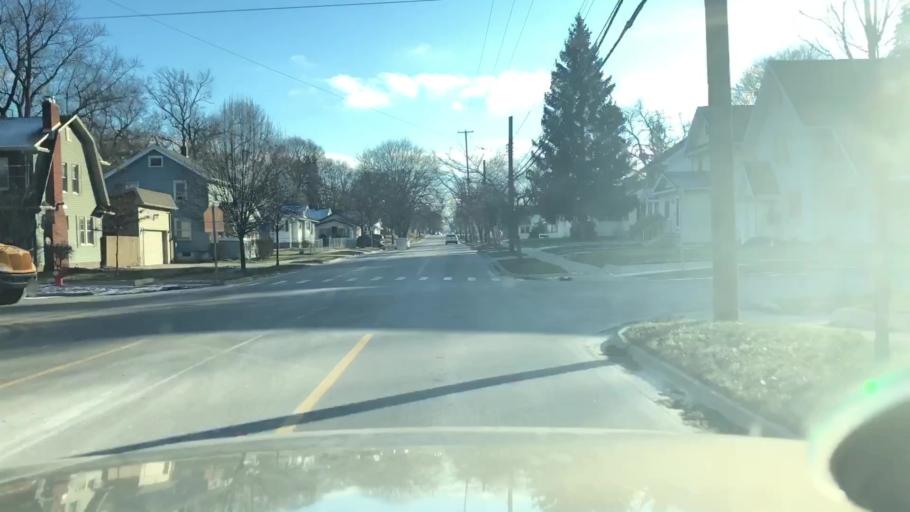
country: US
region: Michigan
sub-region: Jackson County
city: Jackson
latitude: 42.2366
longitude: -84.4233
